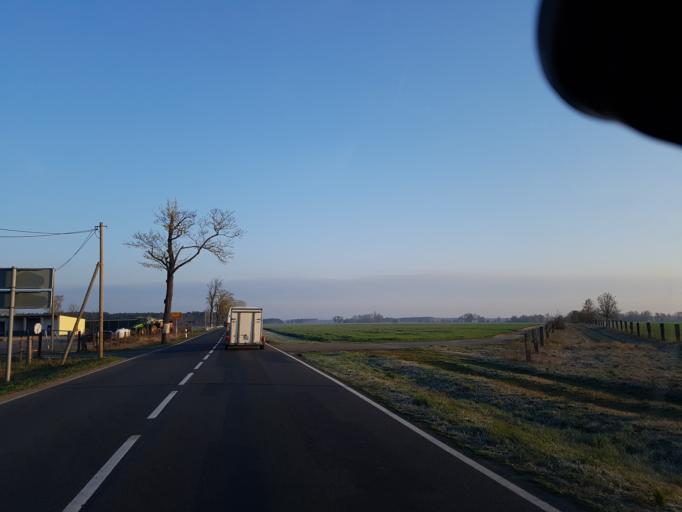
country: DE
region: Saxony-Anhalt
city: Holzdorf
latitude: 51.7995
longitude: 13.1790
